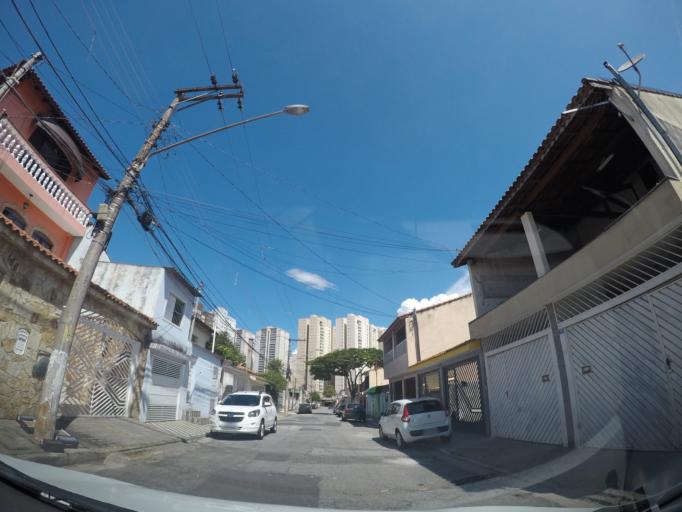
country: BR
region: Sao Paulo
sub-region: Guarulhos
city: Guarulhos
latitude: -23.4585
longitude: -46.5400
